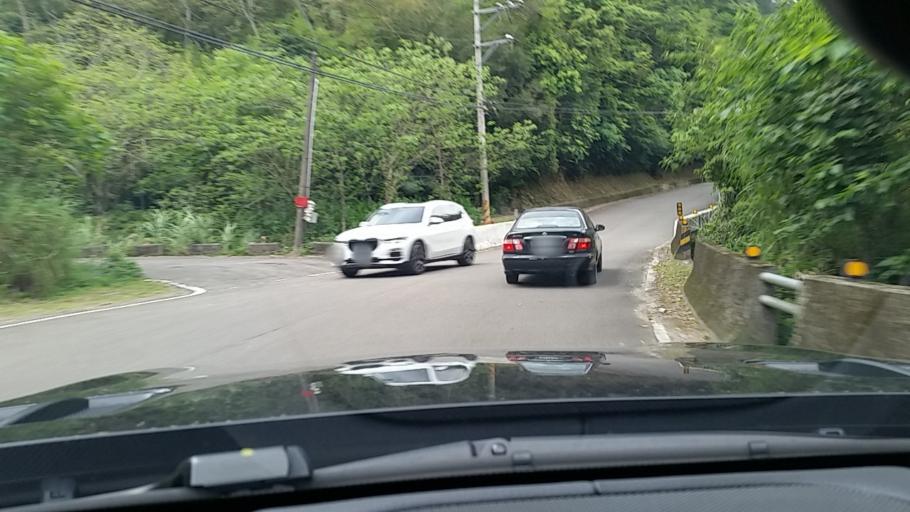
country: TW
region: Taiwan
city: Daxi
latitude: 24.7970
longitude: 121.3021
